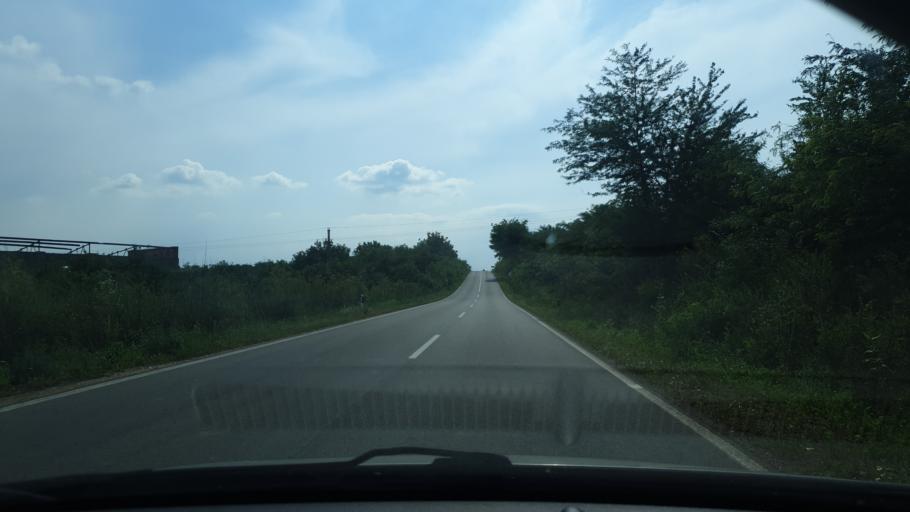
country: RS
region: Central Serbia
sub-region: Pomoravski Okrug
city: Cuprija
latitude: 43.9442
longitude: 21.4188
